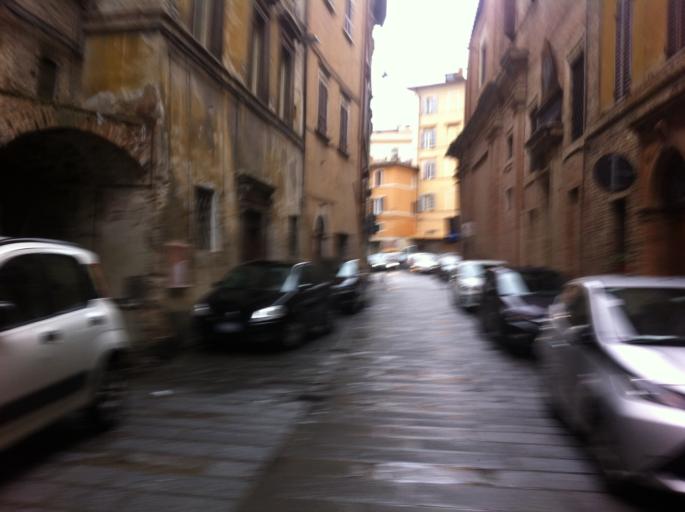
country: IT
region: Umbria
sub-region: Provincia di Perugia
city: Perugia
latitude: 43.1127
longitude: 12.3912
